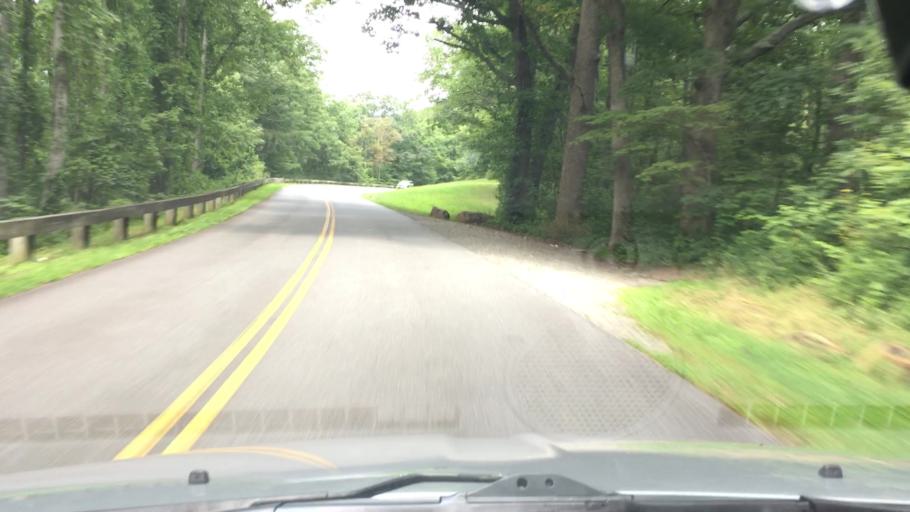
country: US
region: North Carolina
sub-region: Buncombe County
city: Asheville
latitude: 35.6115
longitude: -82.4925
